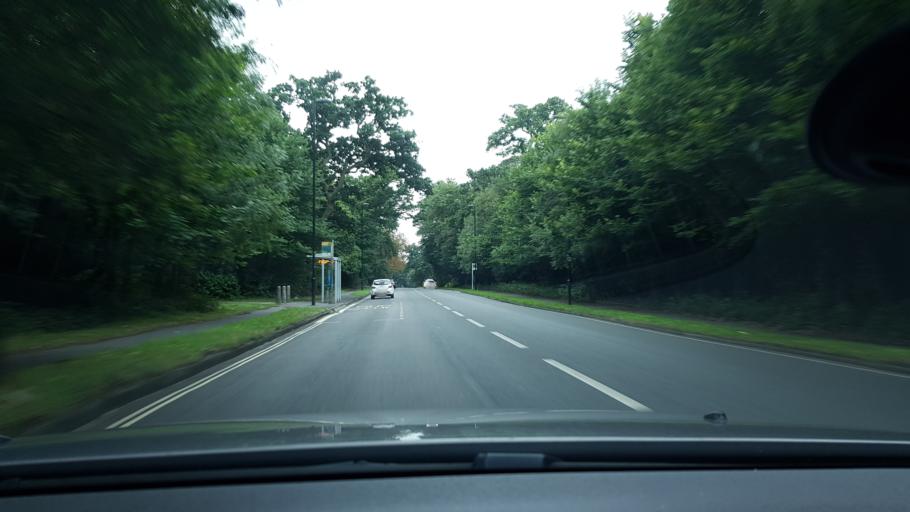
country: GB
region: England
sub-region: Southampton
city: Southampton
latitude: 50.9278
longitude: -1.4056
